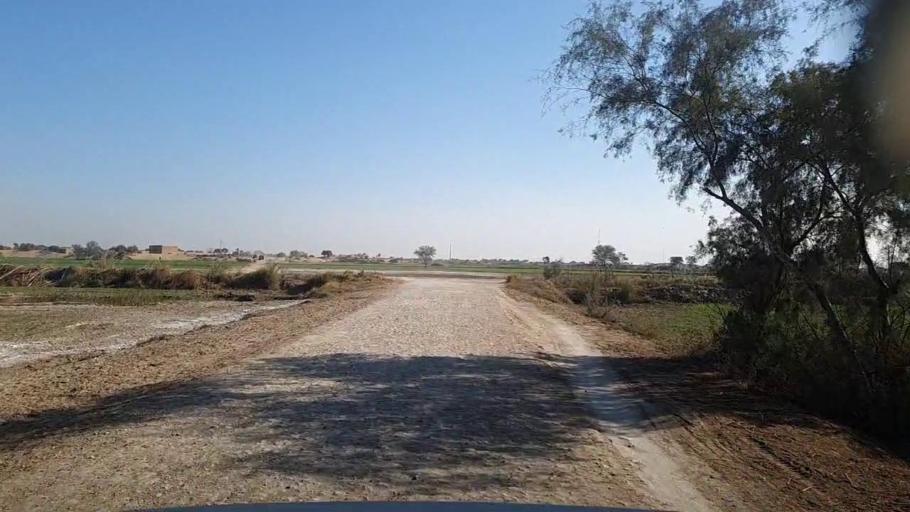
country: PK
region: Sindh
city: Khairpur
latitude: 27.9251
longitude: 69.7366
